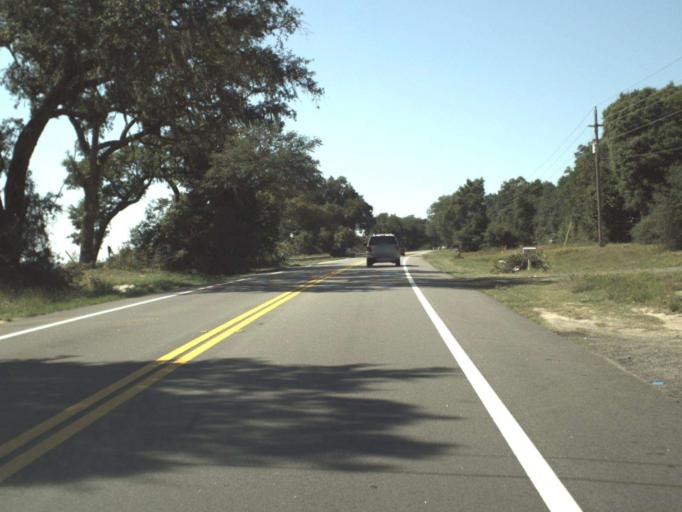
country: US
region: Florida
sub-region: Walton County
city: Miramar Beach
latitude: 30.4659
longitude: -86.3560
